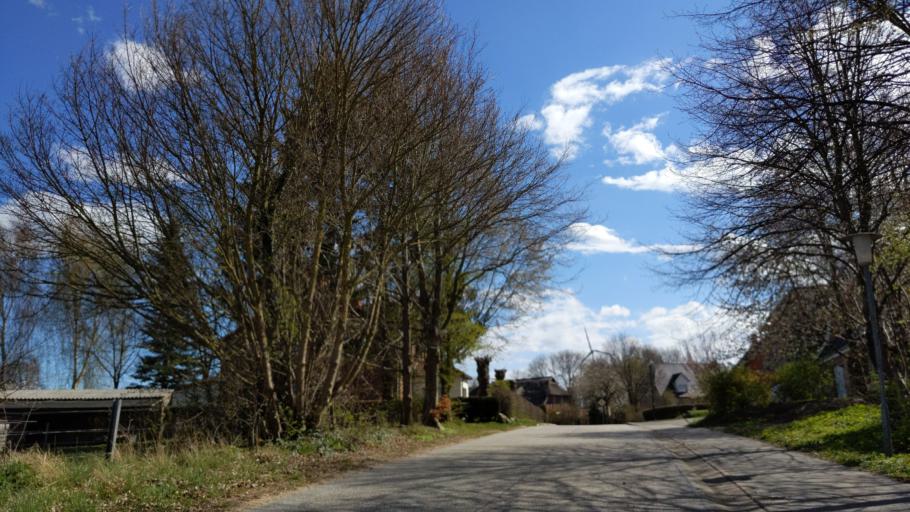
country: DE
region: Mecklenburg-Vorpommern
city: Selmsdorf
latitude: 53.8859
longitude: 10.8895
